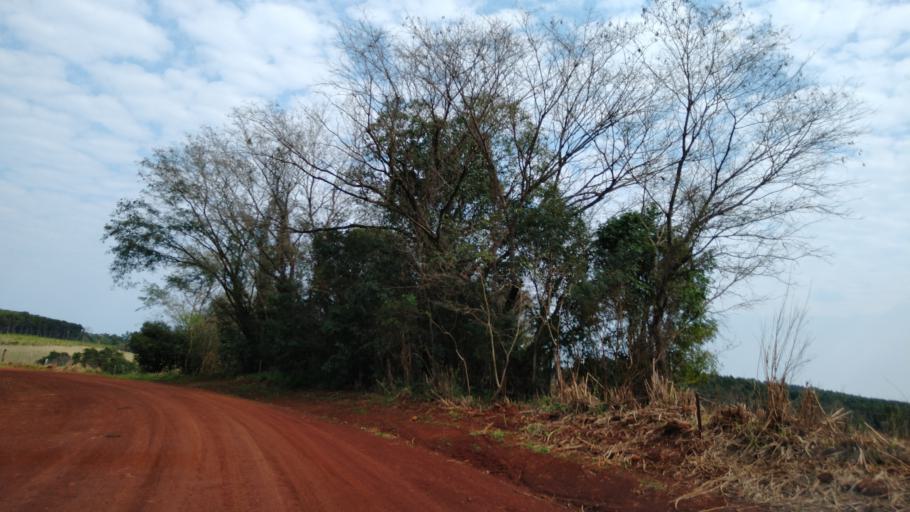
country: AR
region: Misiones
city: Capiovi
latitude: -26.9424
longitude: -55.0677
